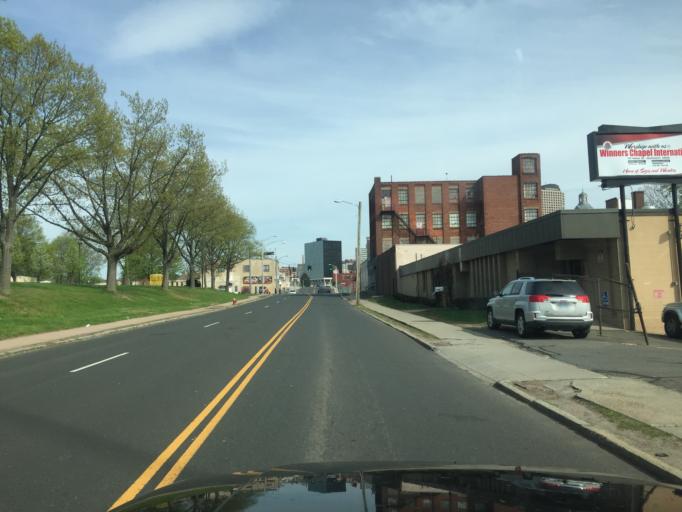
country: US
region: Connecticut
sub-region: Hartford County
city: Hartford
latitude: 41.7739
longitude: -72.6839
